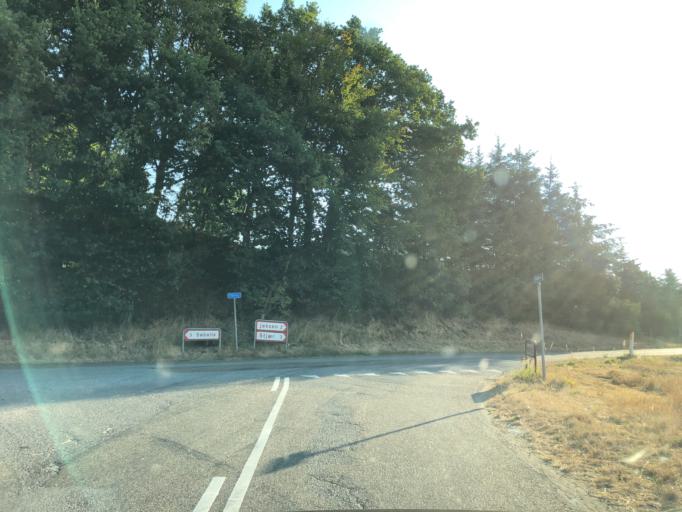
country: DK
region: Central Jutland
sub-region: Skanderborg Kommune
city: Skanderborg
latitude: 56.0966
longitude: 9.9393
